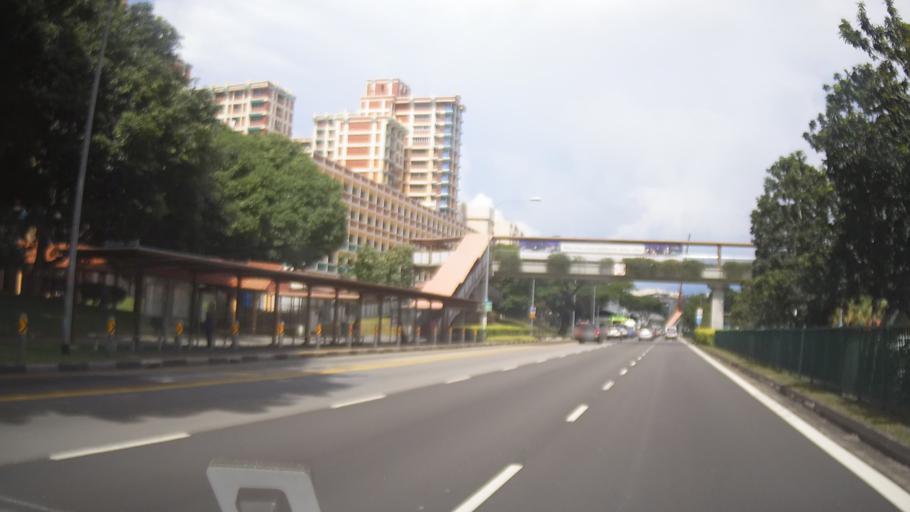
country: SG
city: Singapore
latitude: 1.3310
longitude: 103.9033
